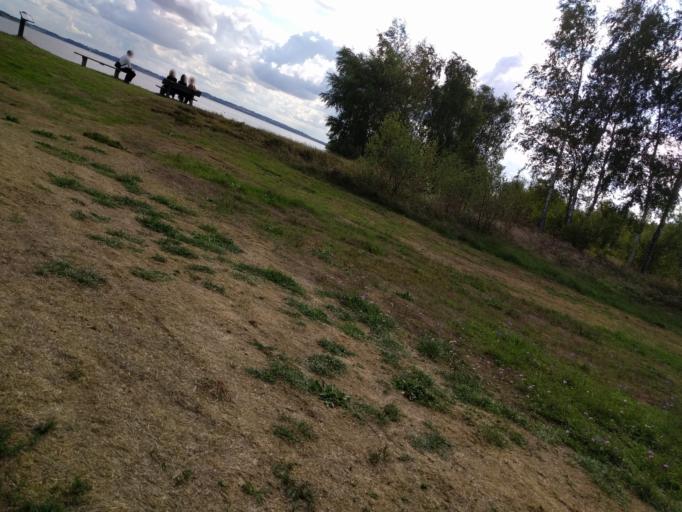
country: DK
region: Central Jutland
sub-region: Skive Kommune
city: Hojslev
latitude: 56.6019
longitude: 9.2871
